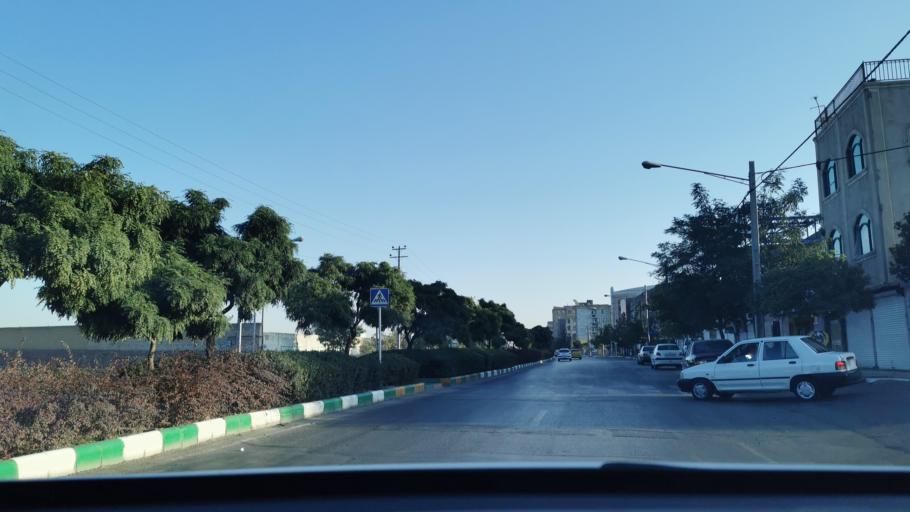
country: IR
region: Razavi Khorasan
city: Mashhad
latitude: 36.3459
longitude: 59.5142
